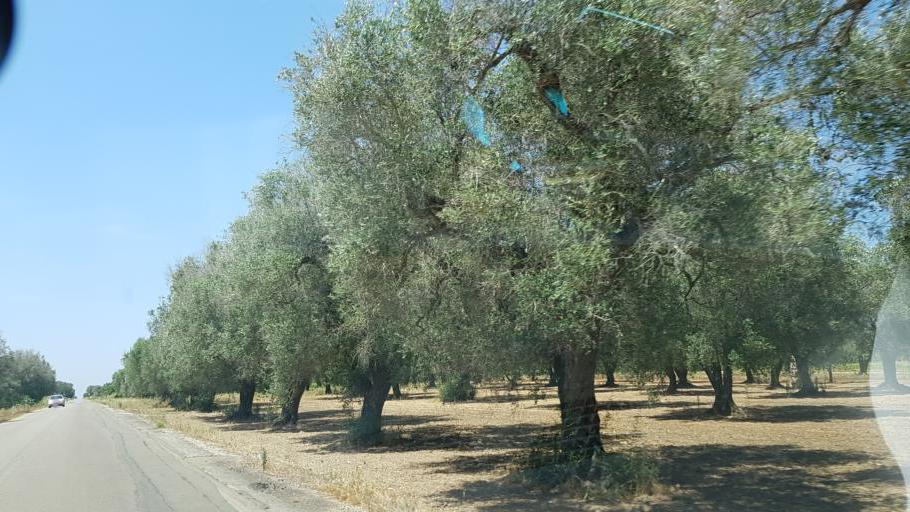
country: IT
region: Apulia
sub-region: Provincia di Brindisi
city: San Donaci
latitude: 40.4750
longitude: 17.8954
